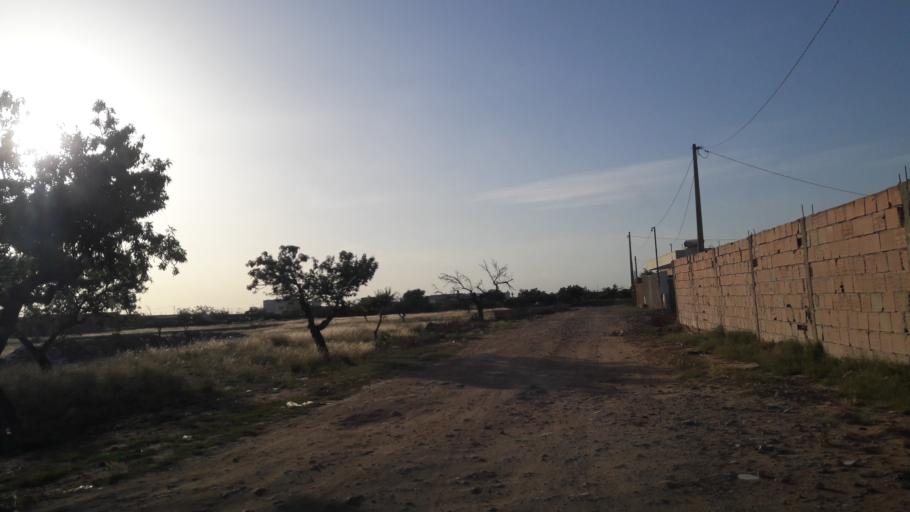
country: TN
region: Safaqis
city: Sfax
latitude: 34.8195
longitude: 10.7380
